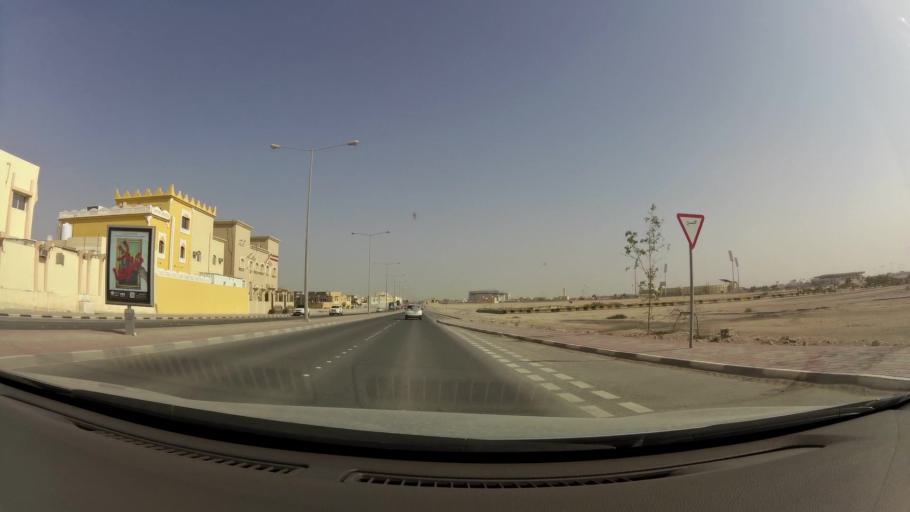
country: QA
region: Baladiyat ar Rayyan
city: Ar Rayyan
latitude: 25.3520
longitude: 51.4393
